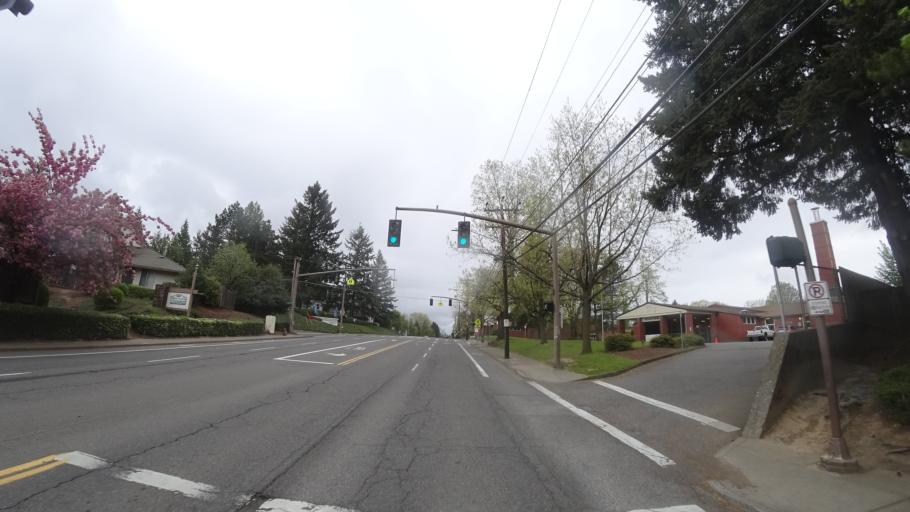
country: US
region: Oregon
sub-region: Washington County
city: Metzger
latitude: 45.4499
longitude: -122.7240
